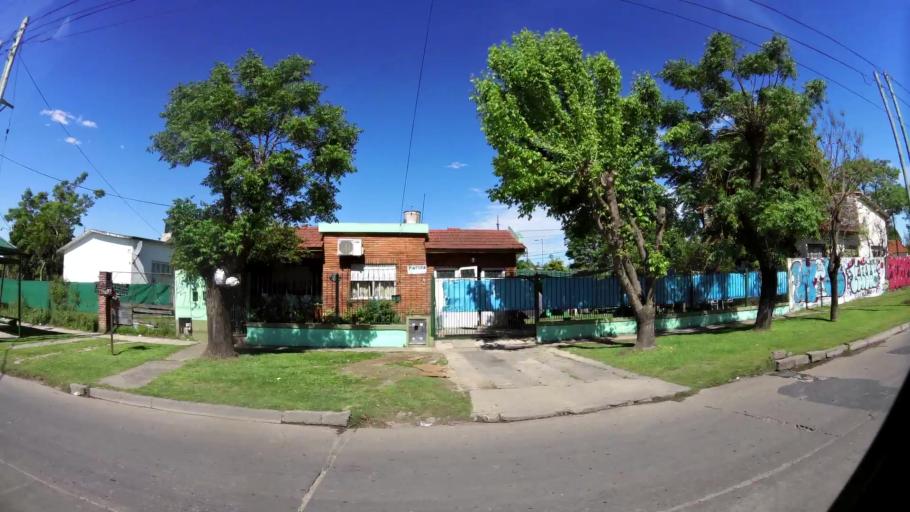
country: AR
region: Buenos Aires
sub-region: Partido de Almirante Brown
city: Adrogue
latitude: -34.7897
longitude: -58.3625
